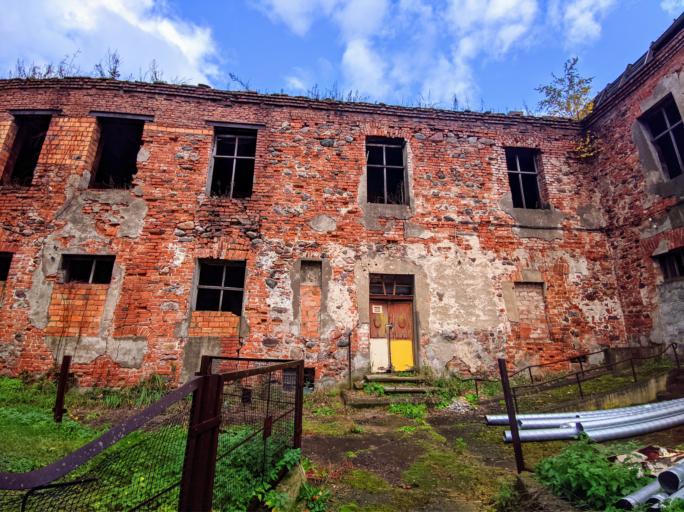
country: PL
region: Lubusz
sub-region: Powiat swiebodzinski
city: Swiebodzin
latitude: 52.2508
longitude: 15.5355
